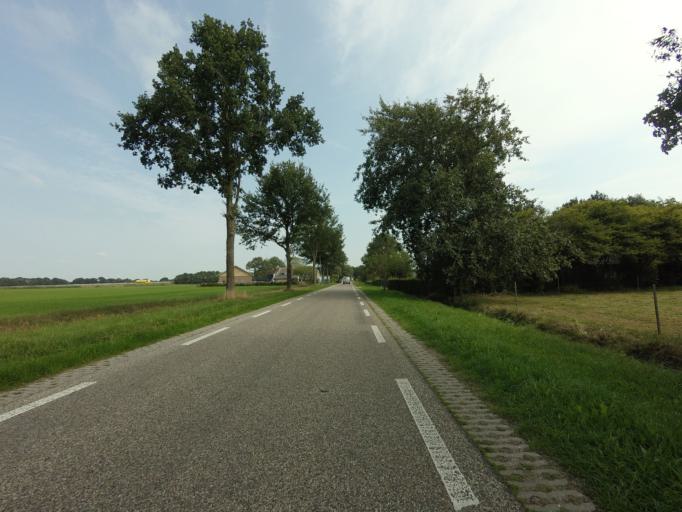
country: NL
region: Drenthe
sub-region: Gemeente Assen
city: Assen
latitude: 52.9677
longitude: 6.6210
